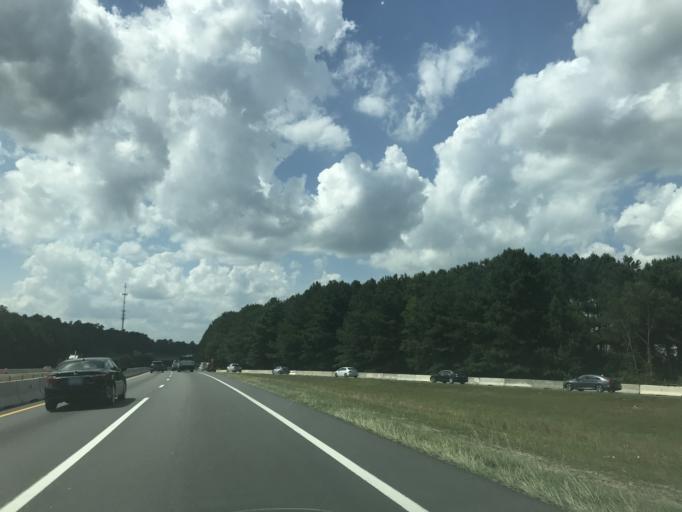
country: US
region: North Carolina
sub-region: Wake County
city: Garner
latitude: 35.6970
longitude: -78.5769
